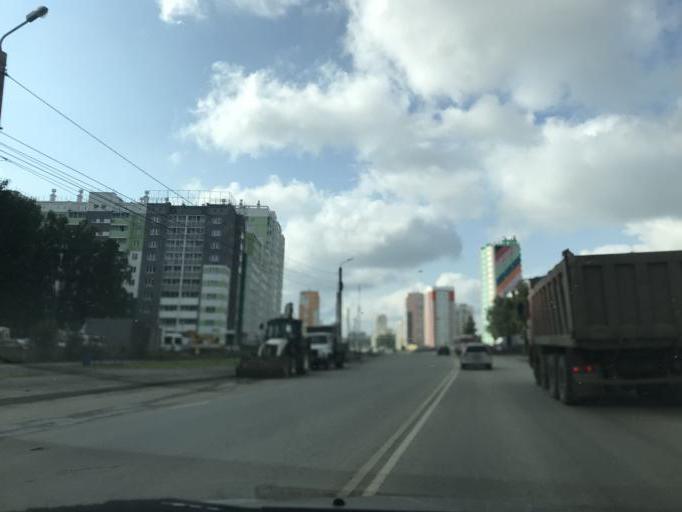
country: RU
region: Chelyabinsk
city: Roshchino
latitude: 55.2132
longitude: 61.2846
